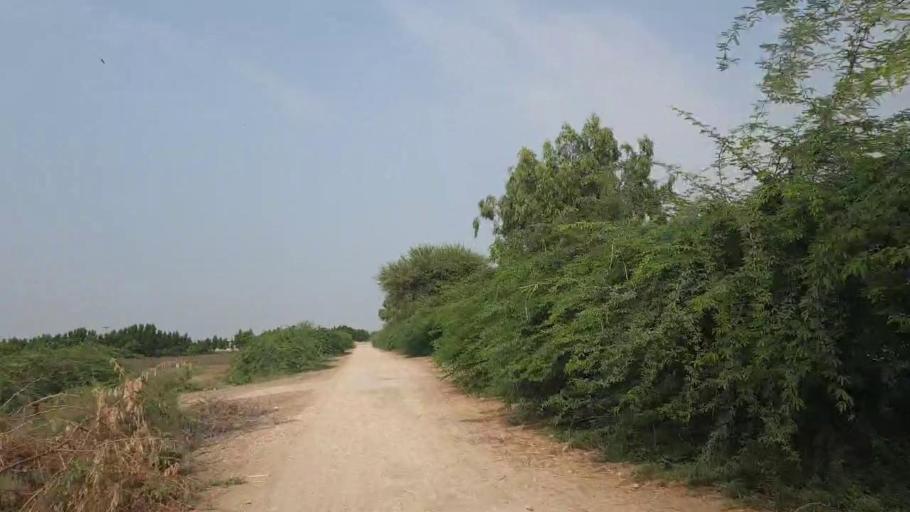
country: PK
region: Sindh
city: Badin
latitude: 24.6011
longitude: 68.7413
